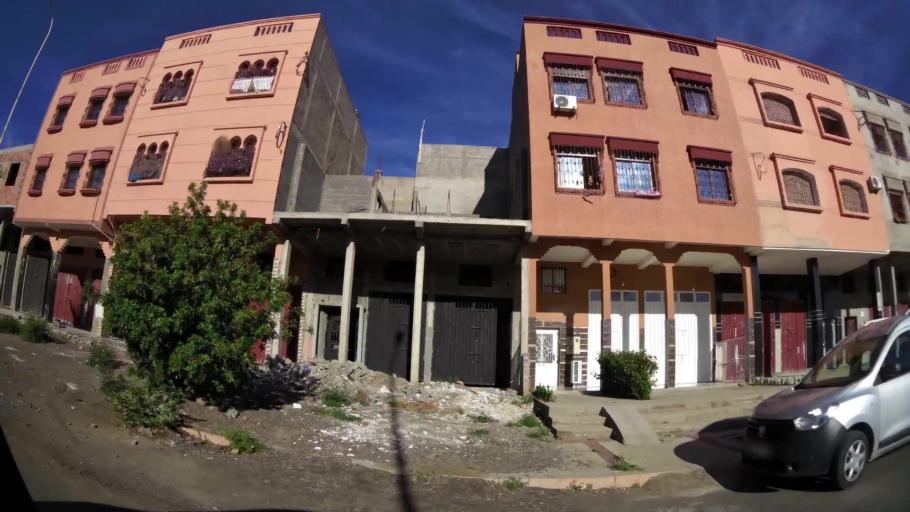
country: MA
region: Marrakech-Tensift-Al Haouz
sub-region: Marrakech
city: Marrakesh
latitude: 31.7521
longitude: -8.1051
